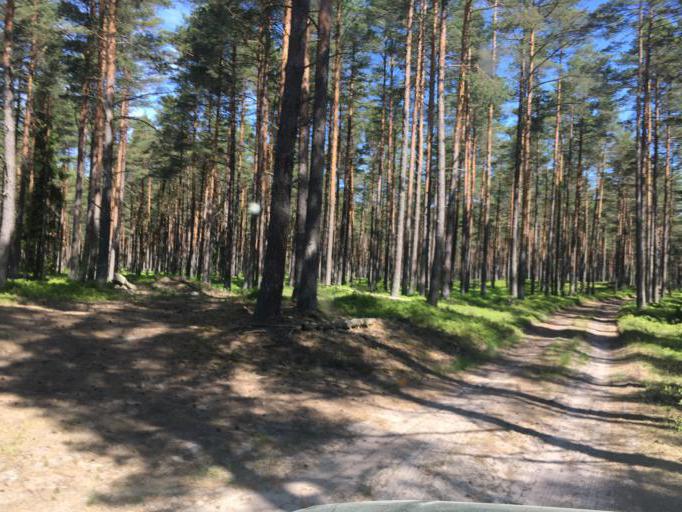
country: LV
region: Ventspils
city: Ventspils
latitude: 57.4740
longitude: 21.6461
